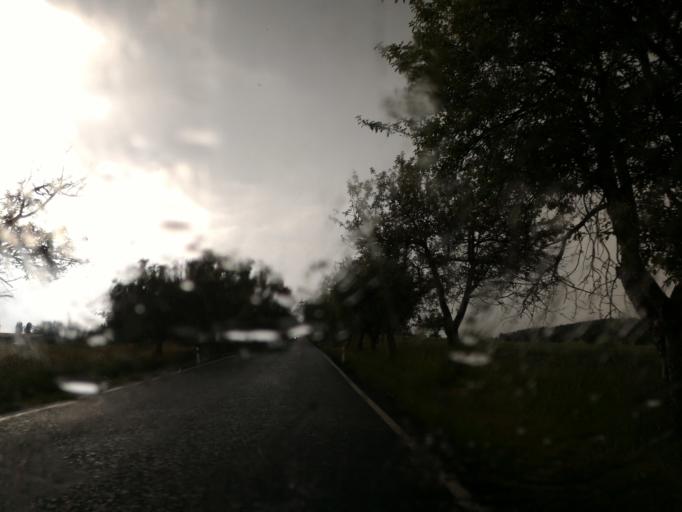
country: CZ
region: Vysocina
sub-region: Okres Jihlava
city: Telc
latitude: 49.1501
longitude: 15.5373
